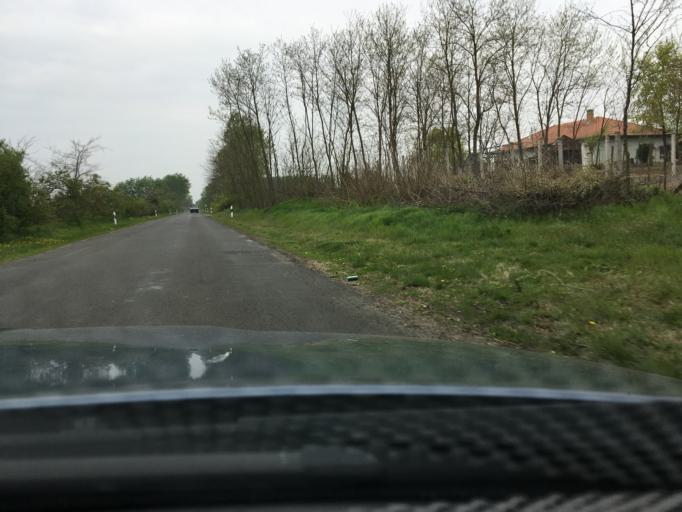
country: HU
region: Hajdu-Bihar
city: Debrecen
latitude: 47.5462
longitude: 21.7056
